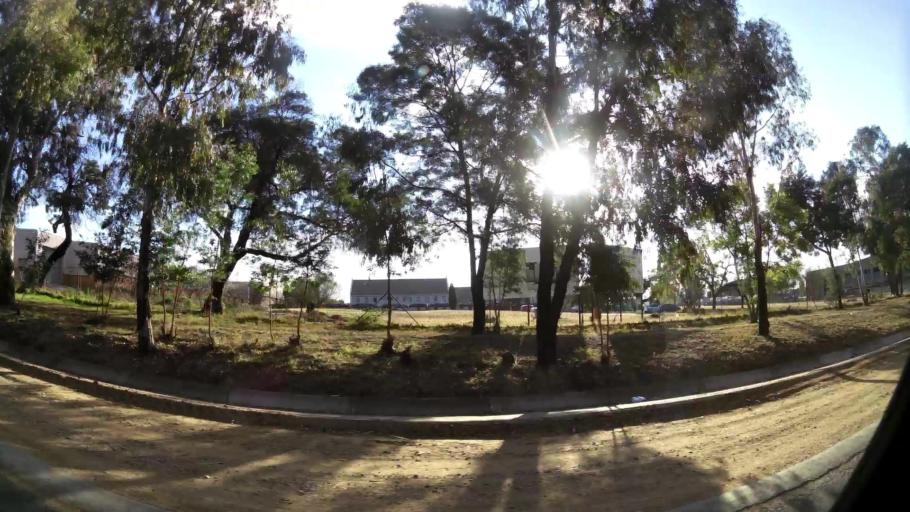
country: ZA
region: Gauteng
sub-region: City of Johannesburg Metropolitan Municipality
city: Midrand
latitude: -25.9677
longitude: 28.1373
